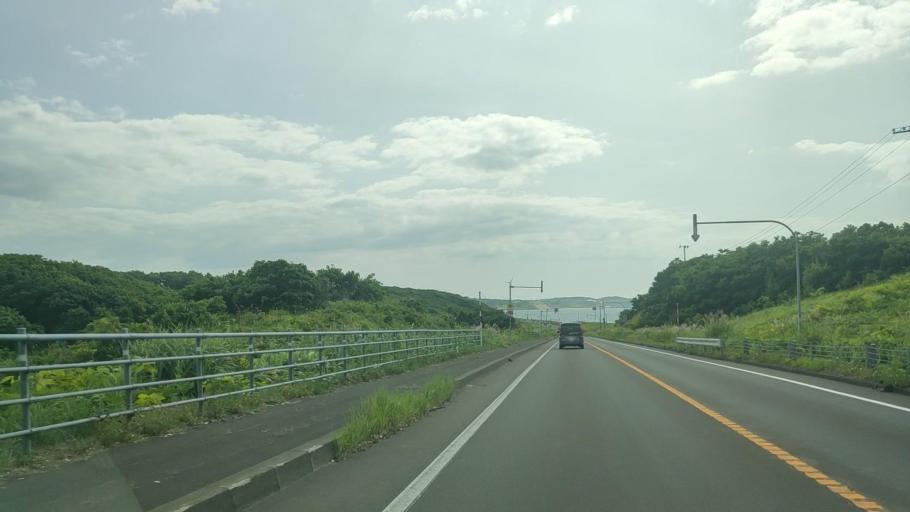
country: JP
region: Hokkaido
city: Rumoi
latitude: 44.3396
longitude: 141.6838
